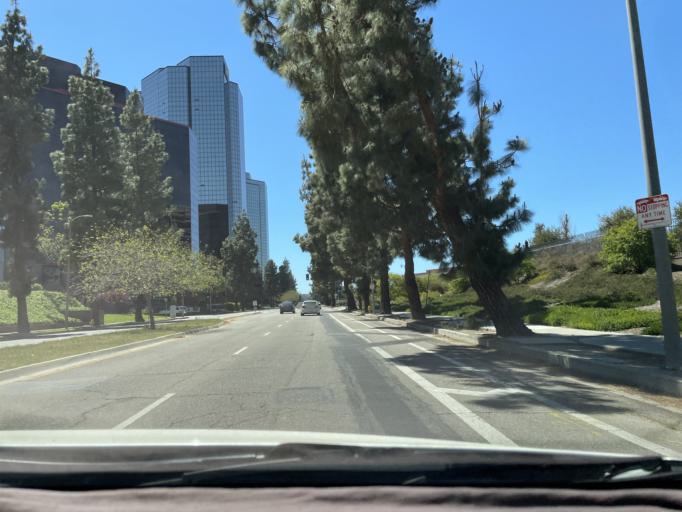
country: US
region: California
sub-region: Los Angeles County
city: Woodland Hills
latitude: 34.1793
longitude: -118.5983
